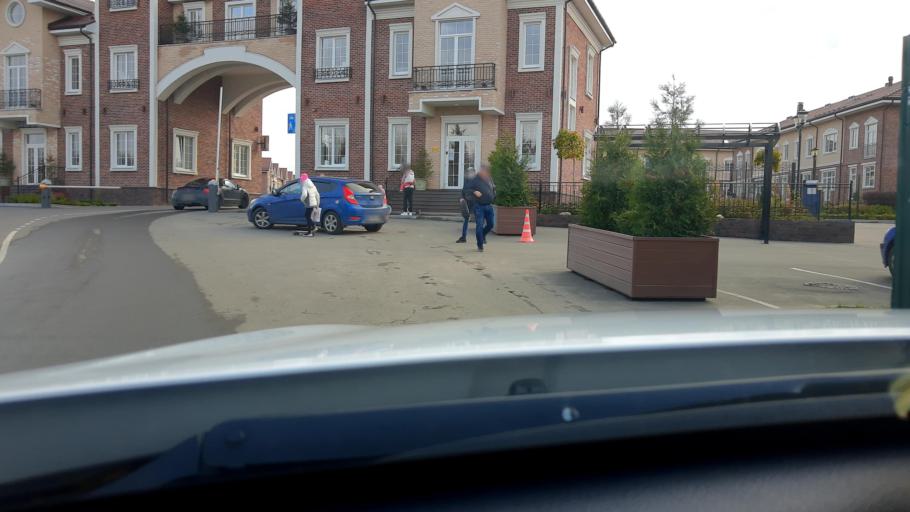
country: RU
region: Moskovskaya
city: Kokoshkino
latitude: 55.5247
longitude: 37.1561
